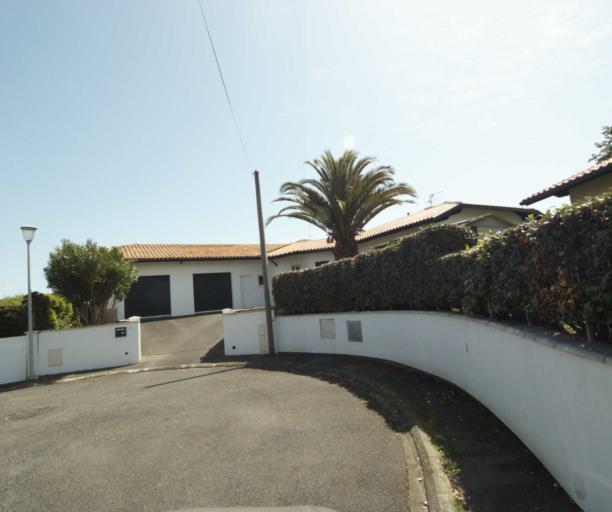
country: FR
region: Aquitaine
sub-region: Departement des Pyrenees-Atlantiques
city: Mouguerre
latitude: 43.4673
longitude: -1.4463
